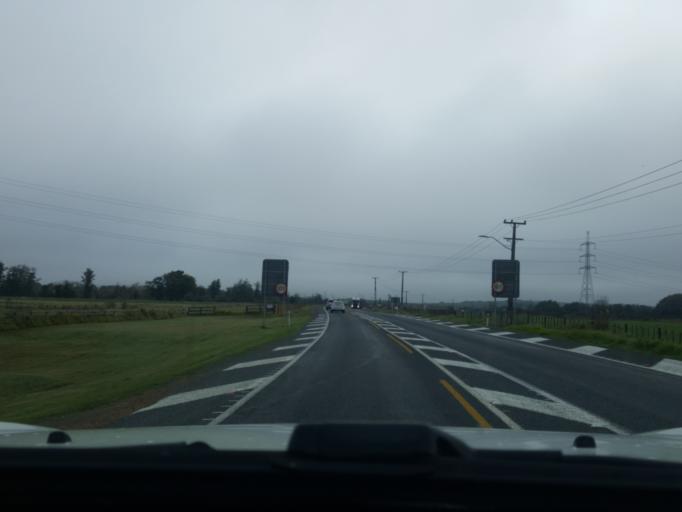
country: NZ
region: Waikato
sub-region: Waikato District
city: Te Kauwhata
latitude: -37.5208
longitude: 175.1621
